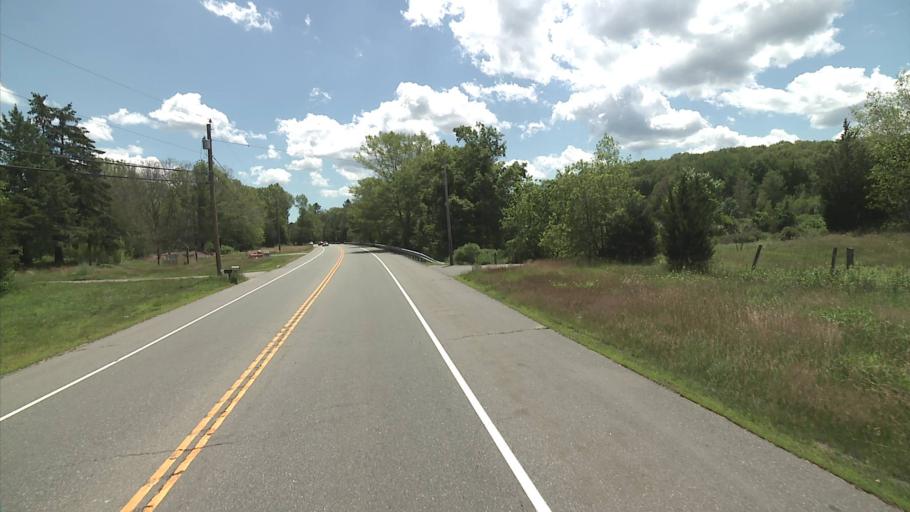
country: US
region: Connecticut
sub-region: New London County
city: Old Mystic
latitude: 41.4563
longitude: -71.9075
